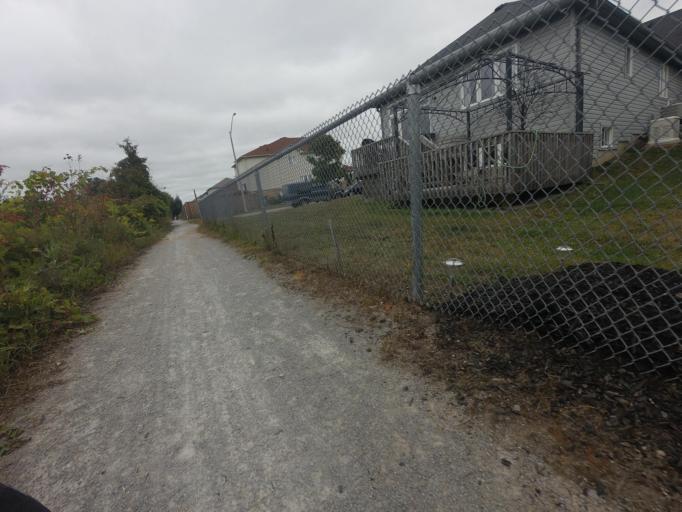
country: CA
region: Ontario
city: Omemee
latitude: 44.3351
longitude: -78.7529
